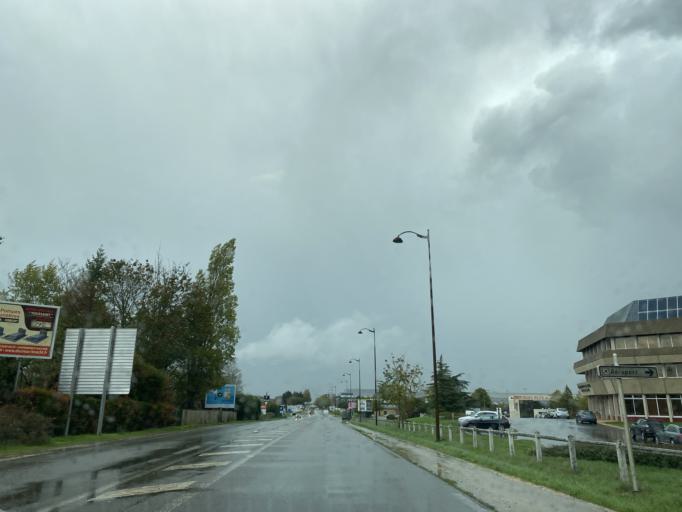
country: FR
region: Centre
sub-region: Departement du Cher
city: Bourges
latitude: 47.0627
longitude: 2.3663
